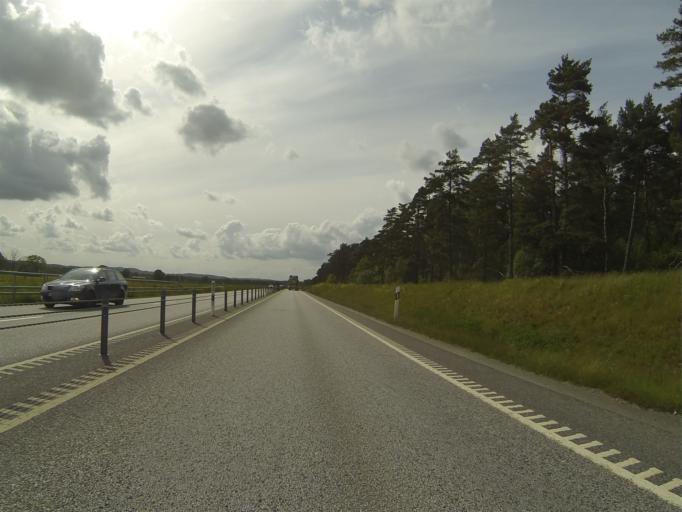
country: SE
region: Skane
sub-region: Sjobo Kommun
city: Blentarp
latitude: 55.6389
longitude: 13.5627
